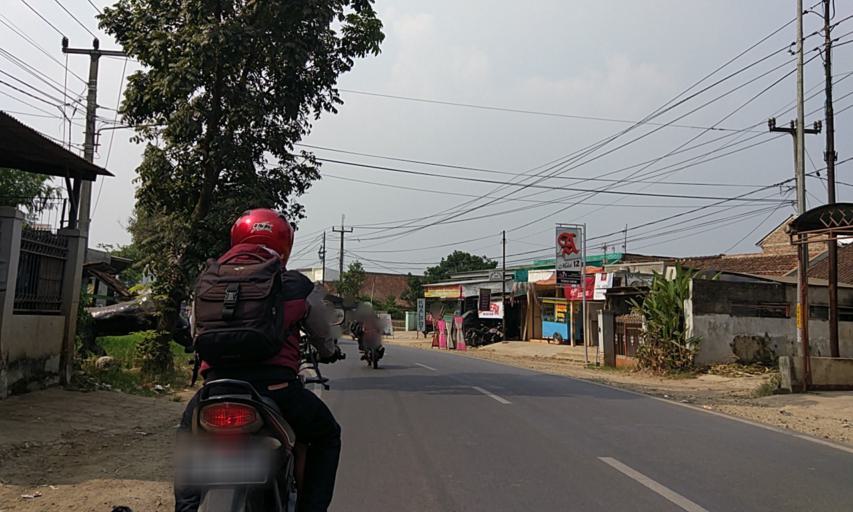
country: ID
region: West Java
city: Banjaran
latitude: -7.0504
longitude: 107.5780
